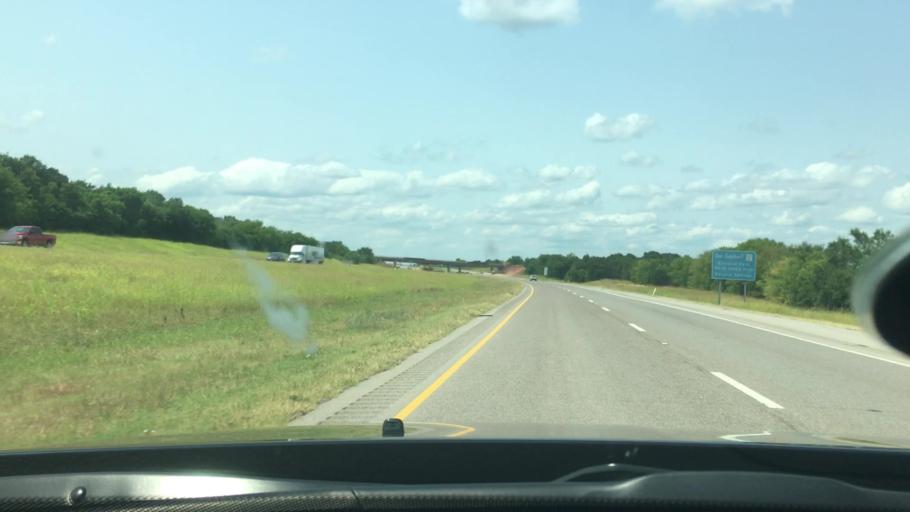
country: US
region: Oklahoma
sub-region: Murray County
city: Davis
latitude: 34.4823
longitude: -97.1581
